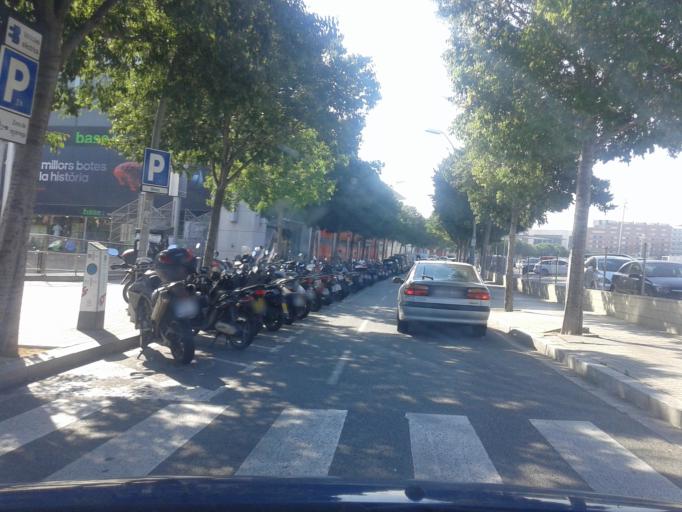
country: ES
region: Catalonia
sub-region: Provincia de Barcelona
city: Sant Andreu de Palomar
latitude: 41.4424
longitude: 2.1974
